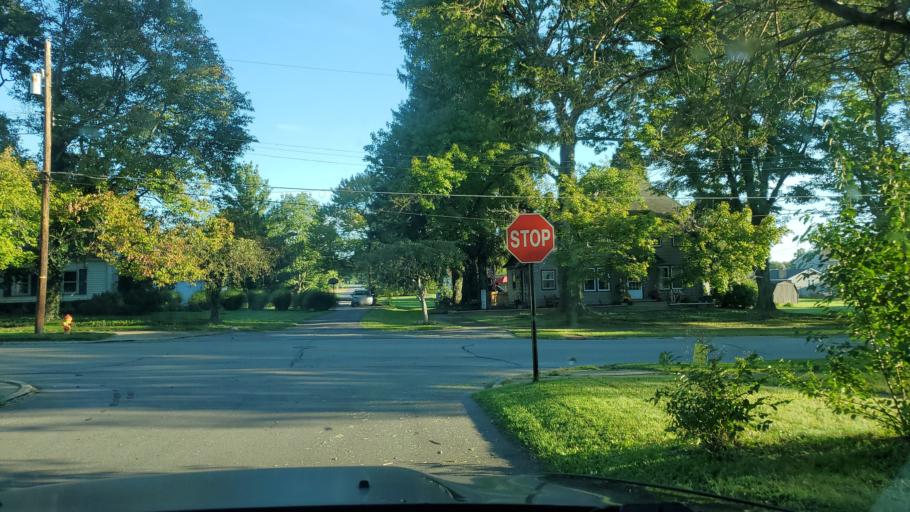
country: US
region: Ohio
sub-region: Mahoning County
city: Poland
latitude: 41.0379
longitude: -80.6113
